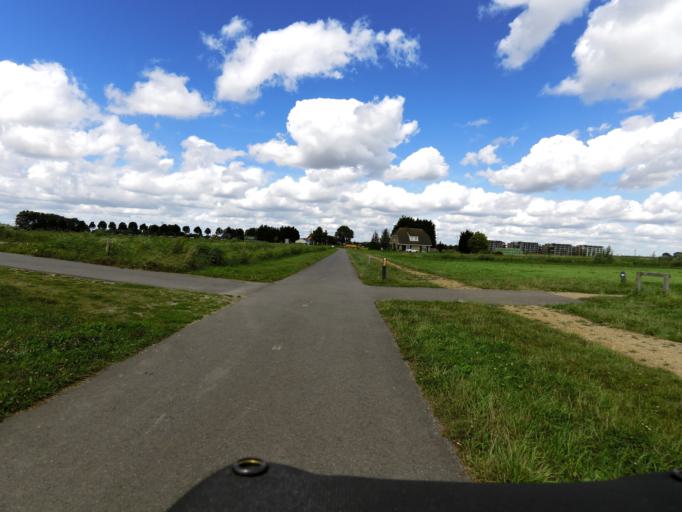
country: NL
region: South Holland
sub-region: Gemeente Oud-Beijerland
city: Oud-Beijerland
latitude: 51.8241
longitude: 4.3692
